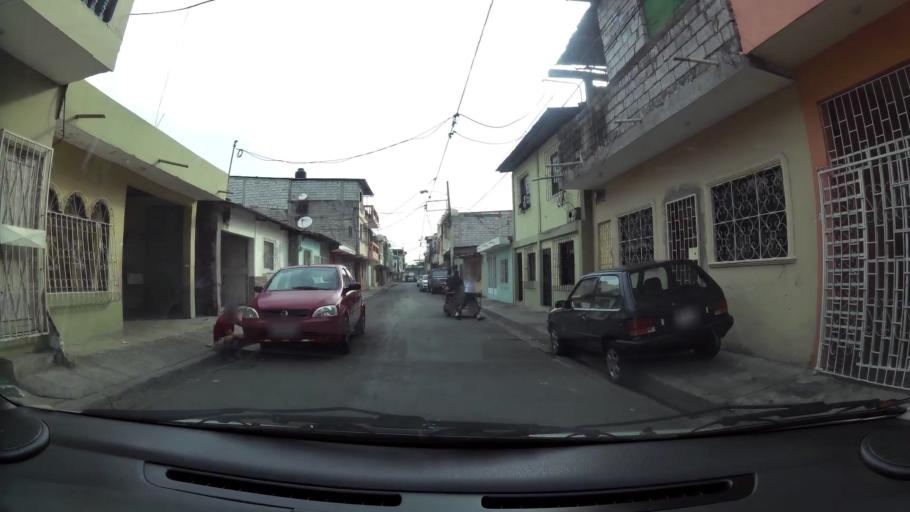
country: EC
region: Guayas
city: Guayaquil
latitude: -2.2514
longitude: -79.8974
